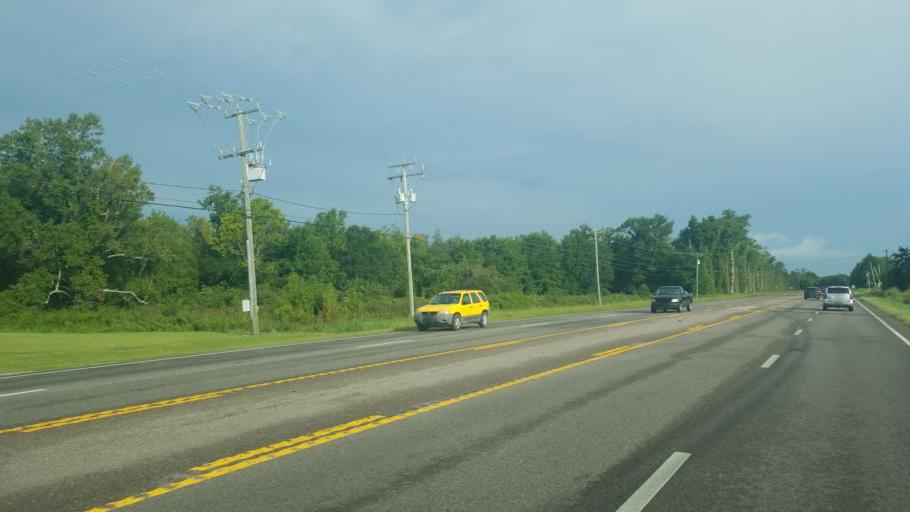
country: US
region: North Carolina
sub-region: Currituck County
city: Currituck
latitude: 36.3286
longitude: -75.9433
